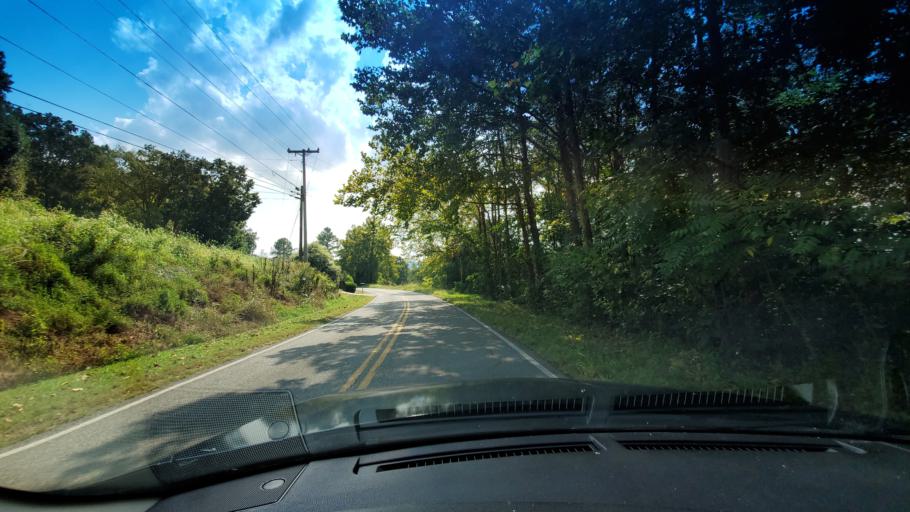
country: US
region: Tennessee
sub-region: Smith County
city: Carthage
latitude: 36.2511
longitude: -85.9653
